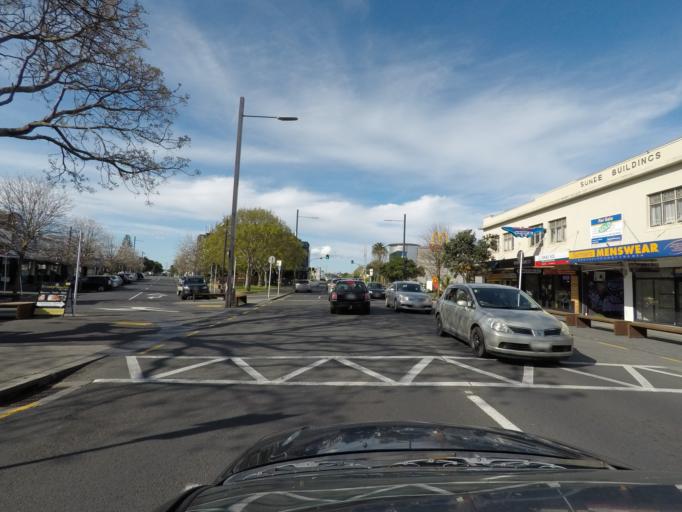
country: NZ
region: Auckland
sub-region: Auckland
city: Waitakere
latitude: -36.9082
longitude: 174.6823
